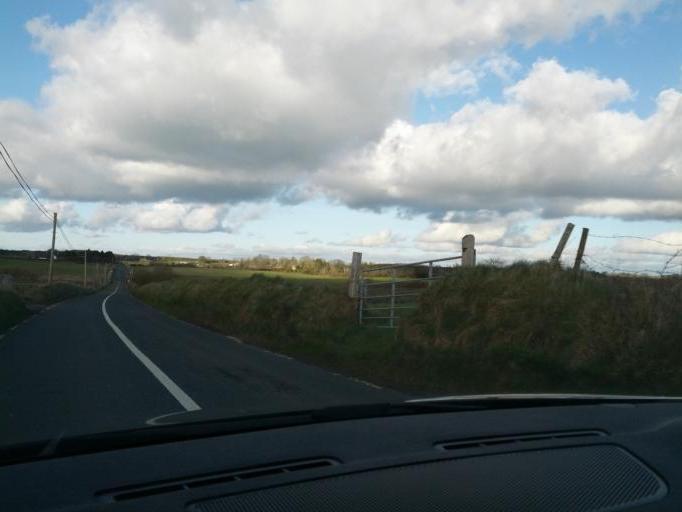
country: IE
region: Connaught
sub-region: Roscommon
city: Castlerea
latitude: 53.6447
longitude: -8.5261
